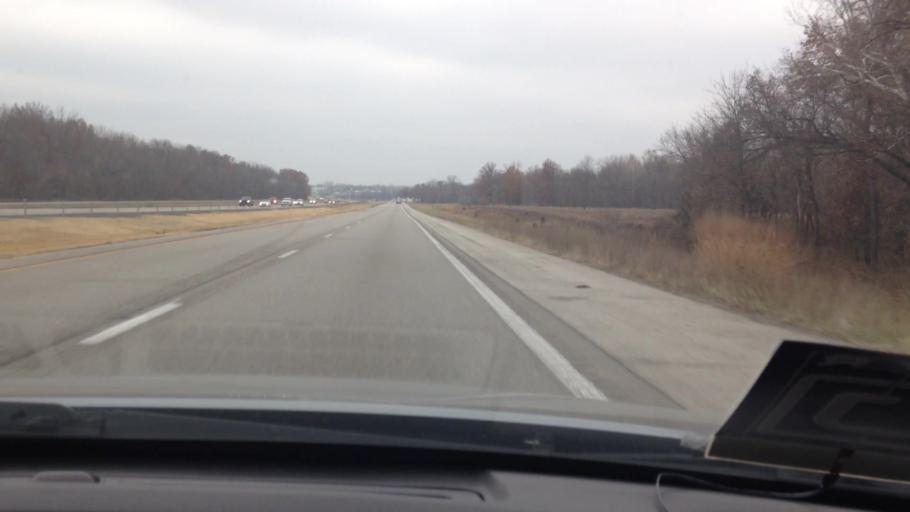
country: US
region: Missouri
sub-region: Cass County
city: Peculiar
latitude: 38.6912
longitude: -94.4272
